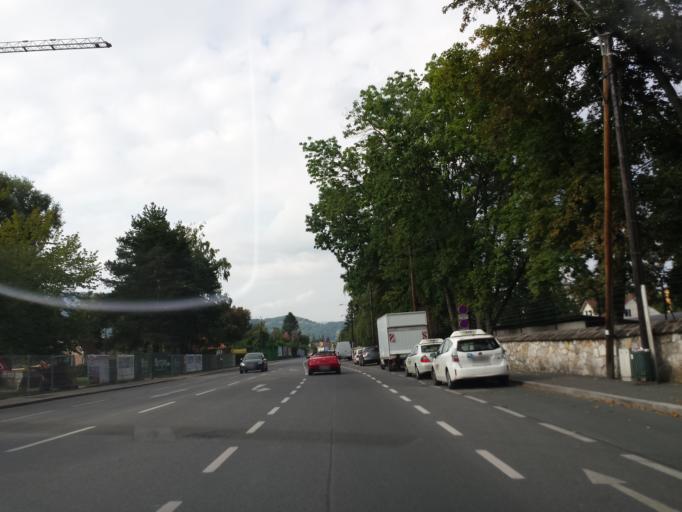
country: AT
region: Styria
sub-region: Graz Stadt
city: Wetzelsdorf
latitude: 47.0533
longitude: 15.3951
